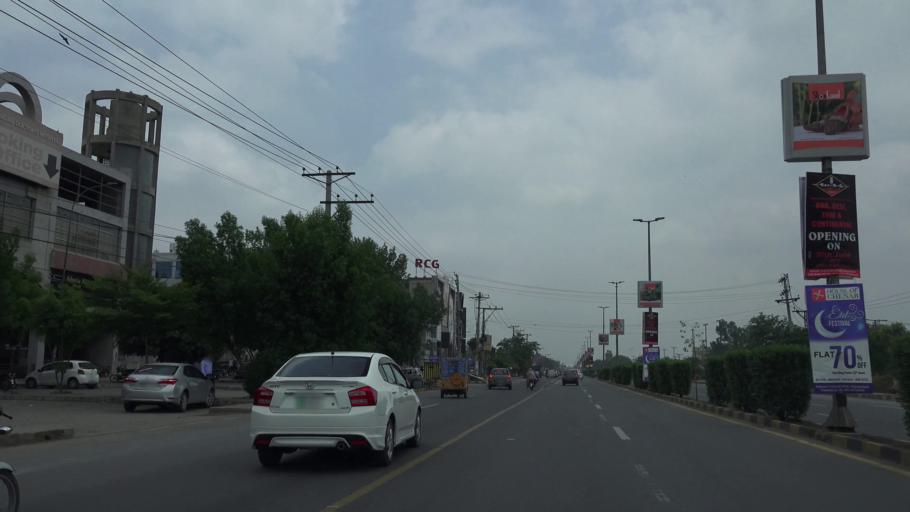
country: PK
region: Punjab
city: Faisalabad
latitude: 31.4058
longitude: 73.1234
